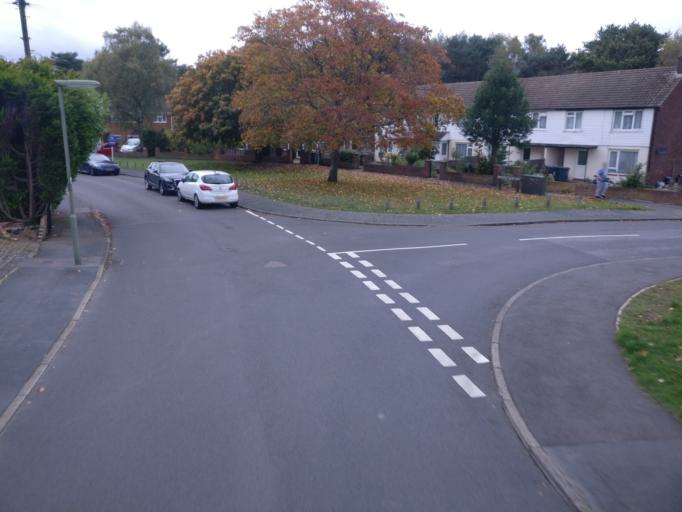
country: GB
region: England
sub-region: Surrey
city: Camberley
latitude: 51.3521
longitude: -0.7259
